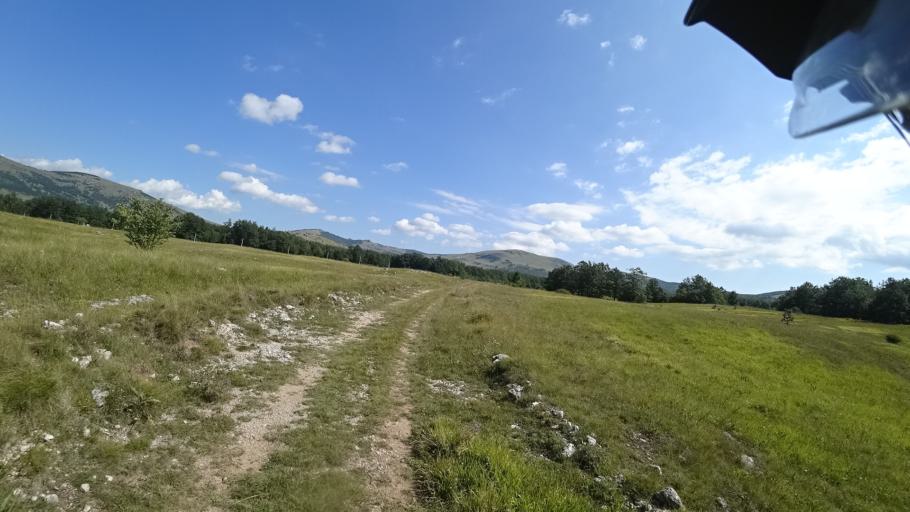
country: HR
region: Zadarska
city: Gracac
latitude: 44.3735
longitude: 15.9603
